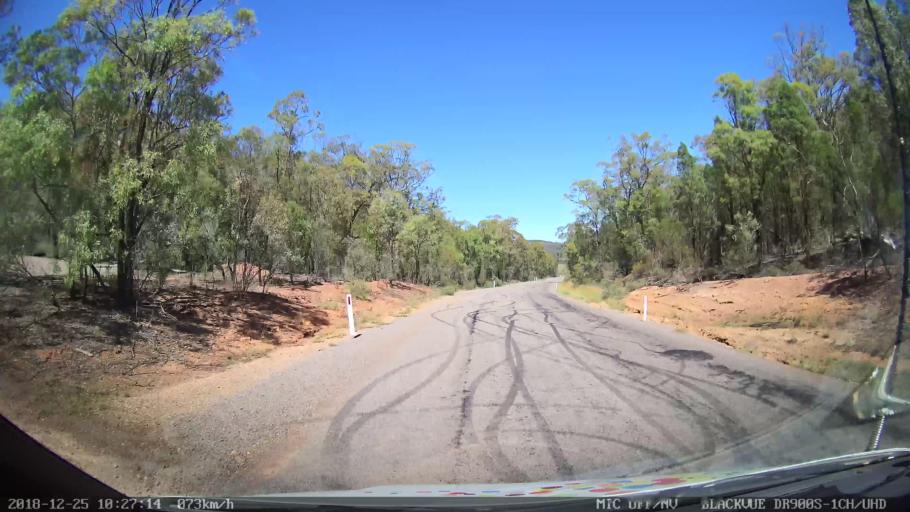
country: AU
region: New South Wales
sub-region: Muswellbrook
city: Denman
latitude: -32.3899
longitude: 150.4751
